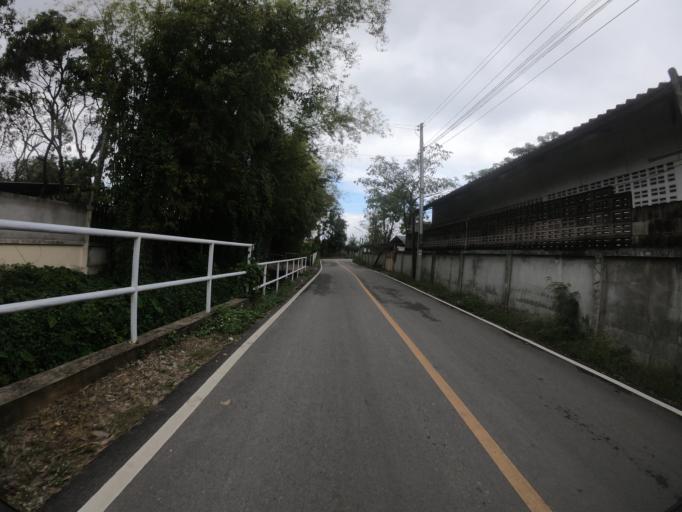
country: TH
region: Chiang Mai
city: Hang Dong
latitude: 18.6963
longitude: 98.9485
